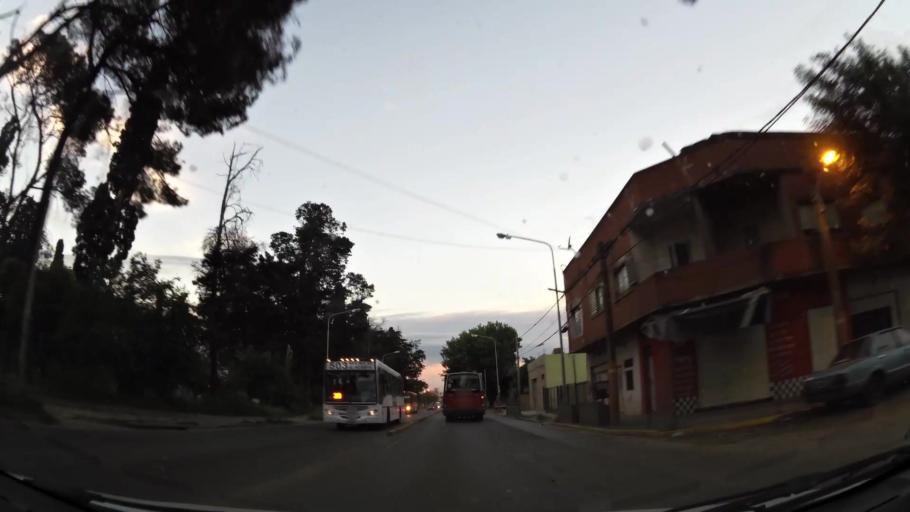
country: AR
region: Buenos Aires
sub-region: Partido de Merlo
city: Merlo
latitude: -34.6823
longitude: -58.7607
